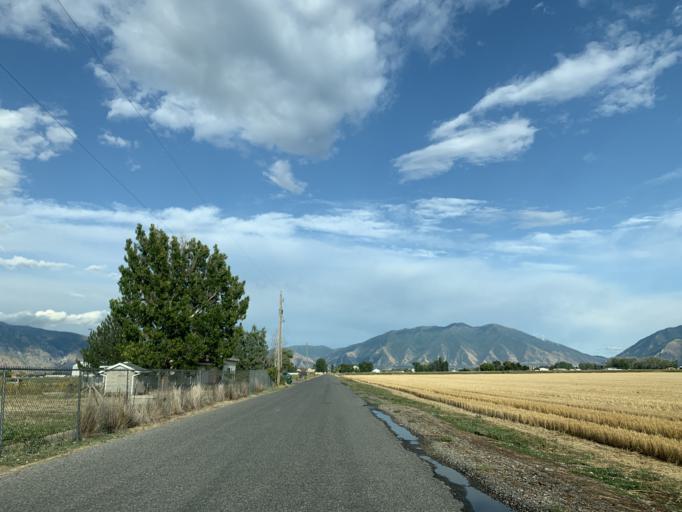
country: US
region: Utah
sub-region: Utah County
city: Benjamin
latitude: 40.1292
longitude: -111.7393
